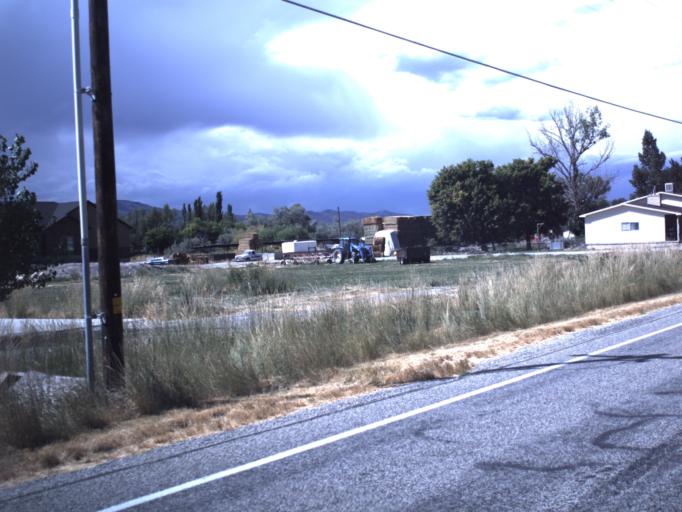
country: US
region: Utah
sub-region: Box Elder County
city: Elwood
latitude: 41.7006
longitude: -112.0901
